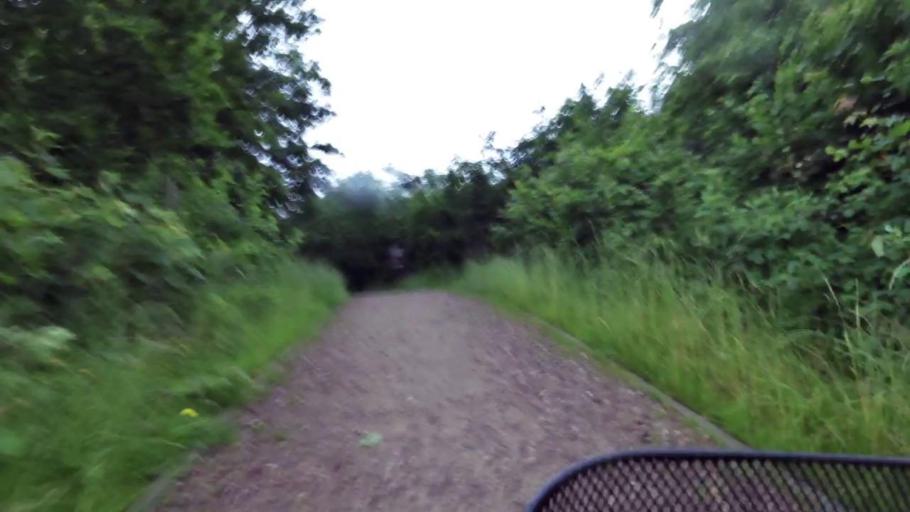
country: PL
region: West Pomeranian Voivodeship
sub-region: Koszalin
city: Koszalin
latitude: 54.1985
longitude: 16.2169
